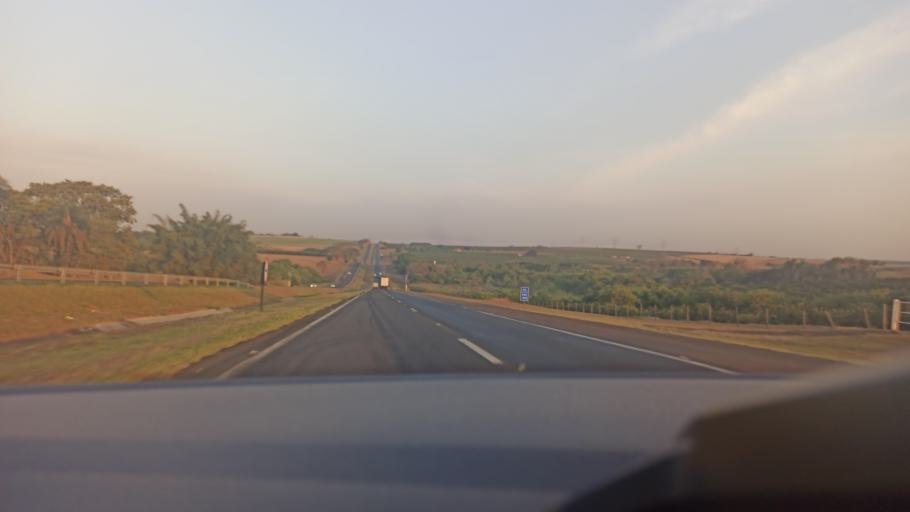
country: BR
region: Sao Paulo
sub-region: Santa Adelia
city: Santa Adelia
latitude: -21.3913
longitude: -48.7204
